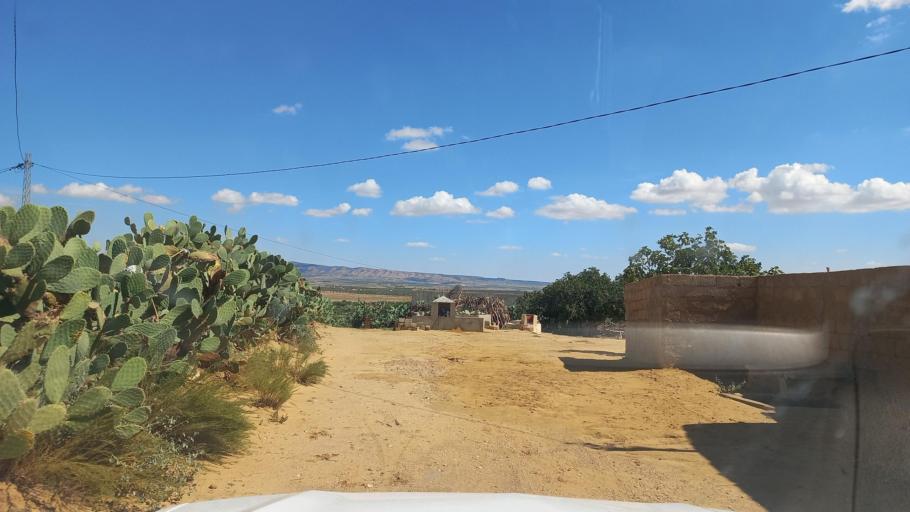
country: TN
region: Al Qasrayn
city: Sbiba
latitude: 35.3613
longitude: 9.0176
